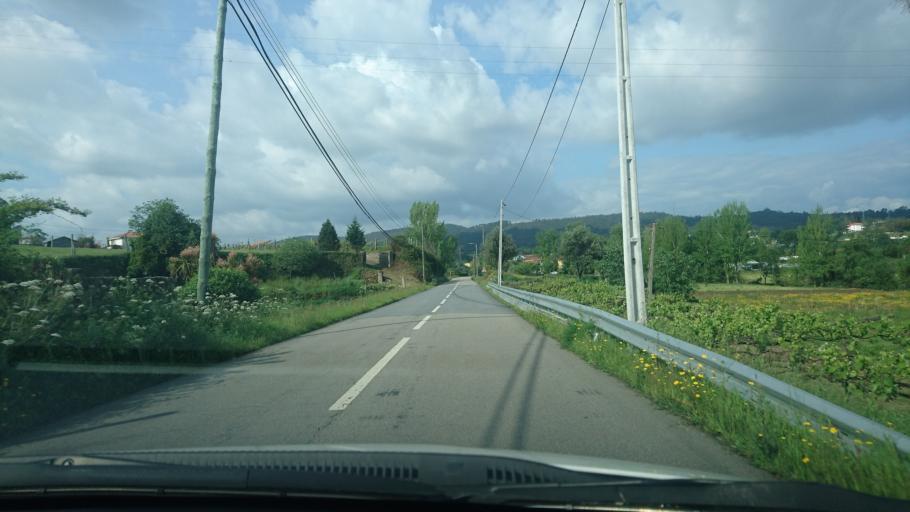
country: PT
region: Porto
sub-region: Paredes
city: Recarei
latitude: 41.1498
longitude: -8.4162
